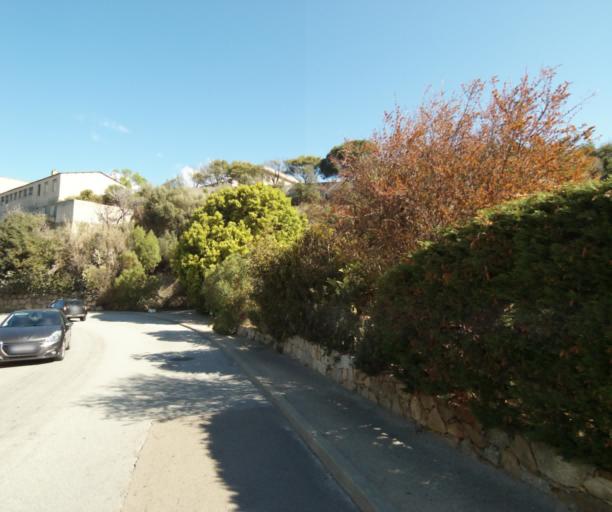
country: FR
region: Corsica
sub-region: Departement de la Corse-du-Sud
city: Propriano
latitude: 41.6722
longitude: 8.9055
